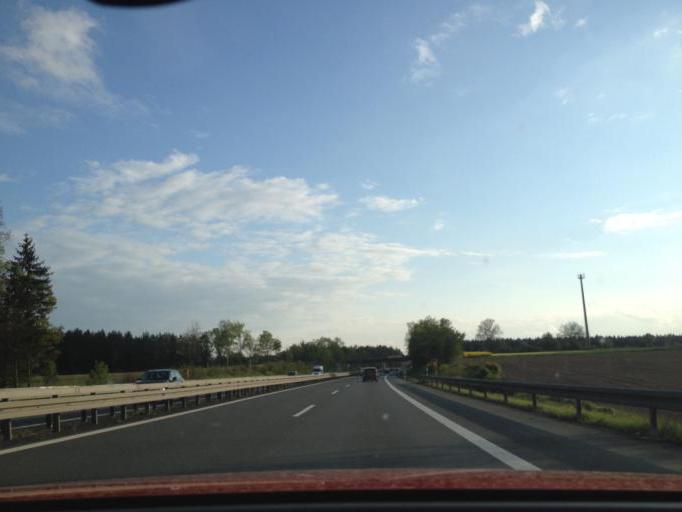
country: DE
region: Bavaria
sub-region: Upper Palatinate
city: Wiesau
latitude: 49.8851
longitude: 12.2106
